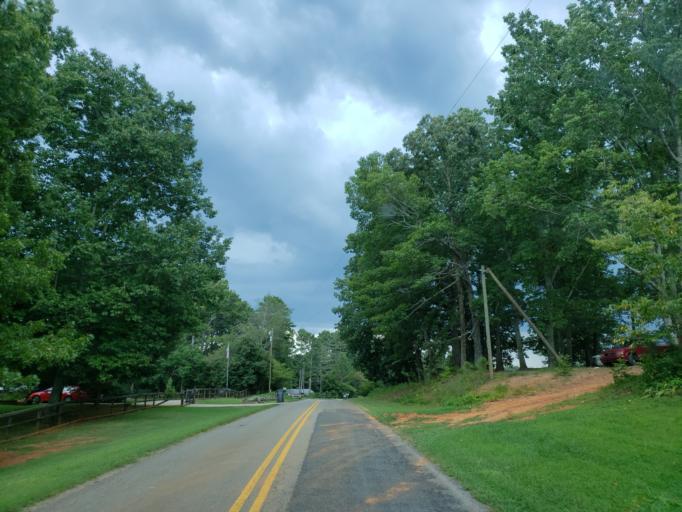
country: US
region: Georgia
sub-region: Pickens County
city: Jasper
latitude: 34.3883
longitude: -84.4661
